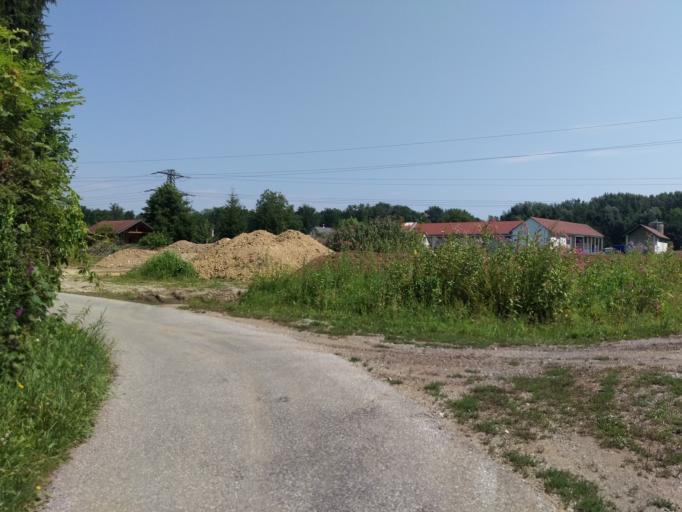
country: AT
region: Styria
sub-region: Politischer Bezirk Graz-Umgebung
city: Kalsdorf bei Graz
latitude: 46.9645
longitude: 15.4827
